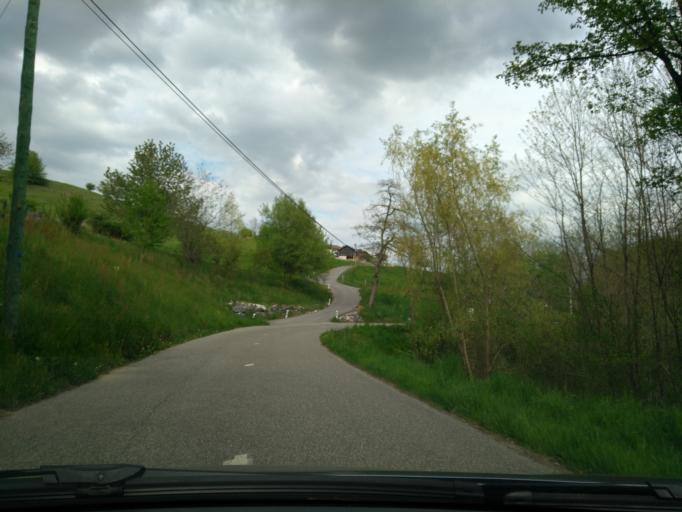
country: FR
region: Rhone-Alpes
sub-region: Departement de la Haute-Savoie
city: Rumilly
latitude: 45.8425
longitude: 5.9116
